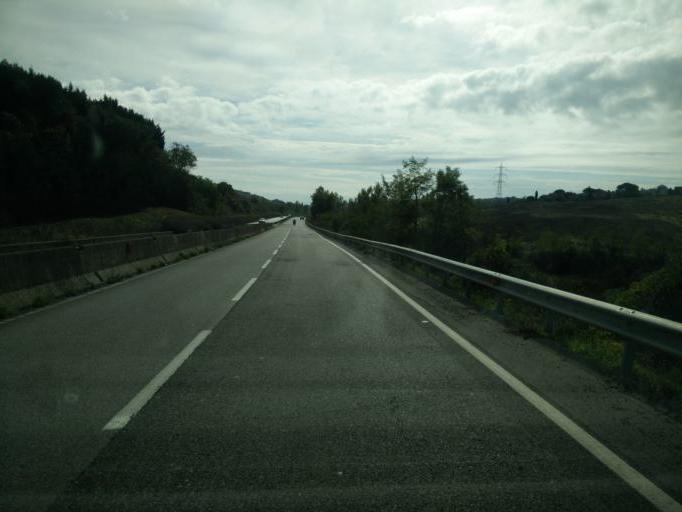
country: IT
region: Tuscany
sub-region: Provincia di Siena
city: Belverde
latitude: 43.3304
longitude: 11.2926
